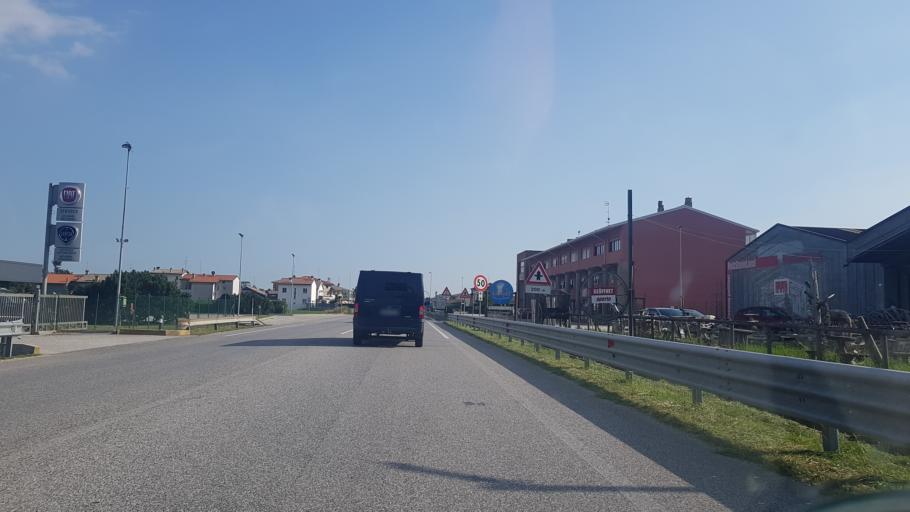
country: IT
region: Friuli Venezia Giulia
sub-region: Provincia di Udine
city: Gemona
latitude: 46.2831
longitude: 13.1098
